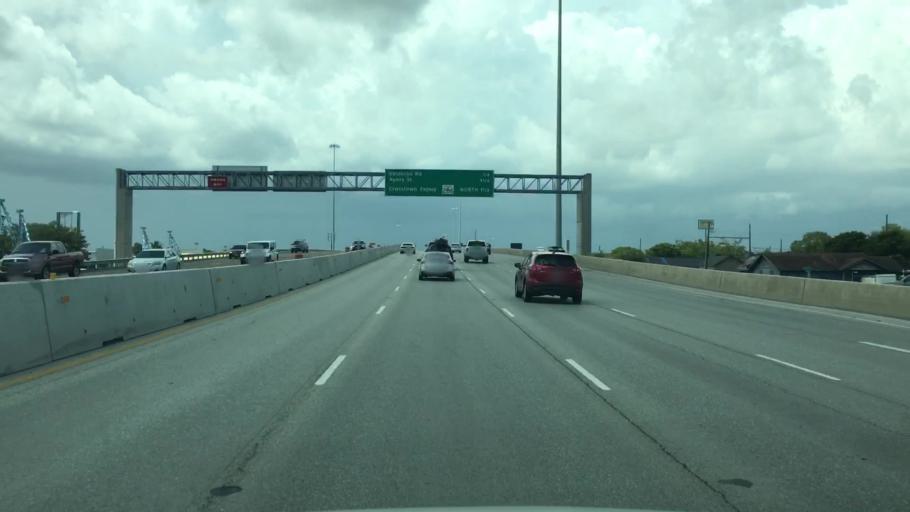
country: US
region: Texas
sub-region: Nueces County
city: Corpus Christi
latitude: 27.7240
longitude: -97.4034
